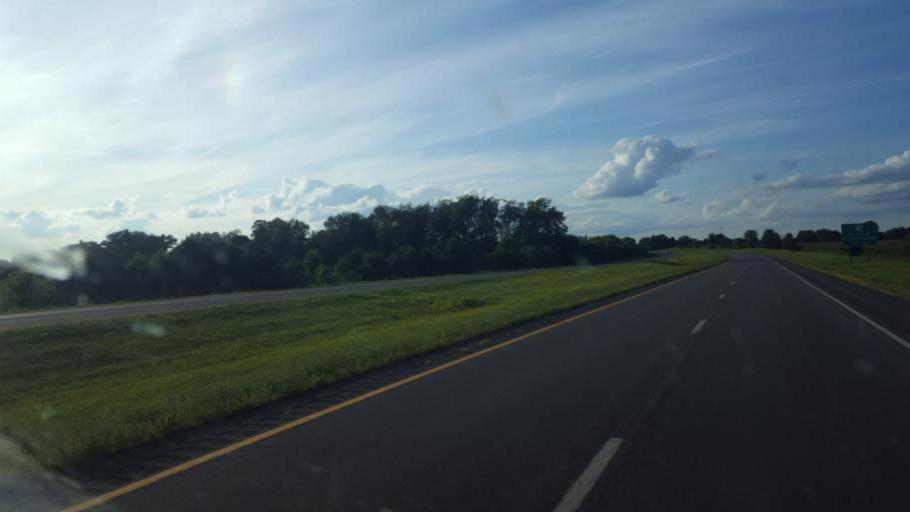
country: US
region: Ohio
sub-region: Knox County
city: Fredericktown
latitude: 40.4622
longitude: -82.5464
